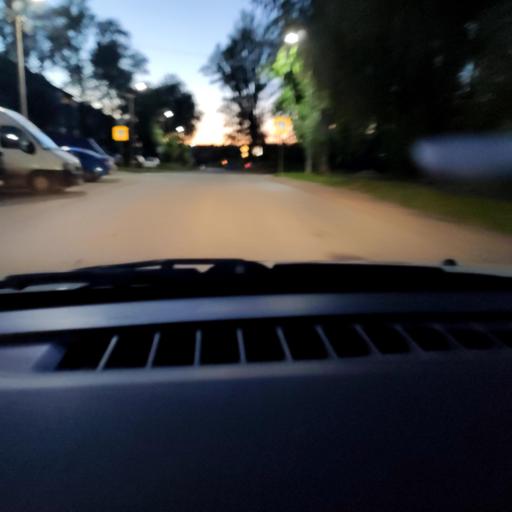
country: RU
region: Perm
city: Zvezdnyy
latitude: 57.7362
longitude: 56.3219
